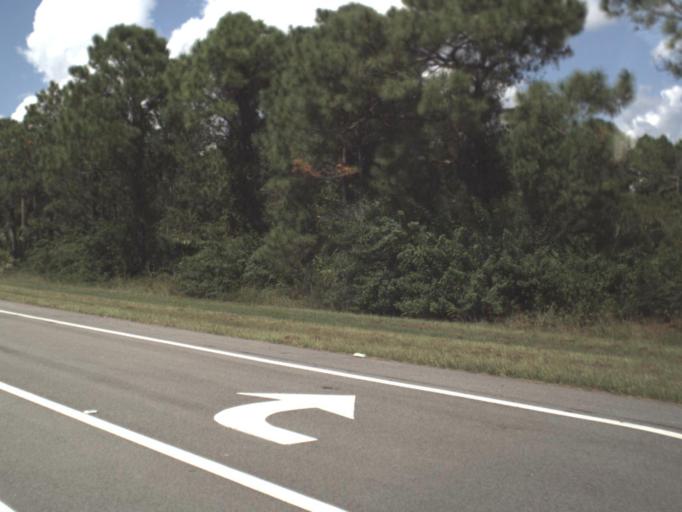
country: US
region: Florida
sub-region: Lee County
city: Gateway
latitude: 26.5860
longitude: -81.7234
